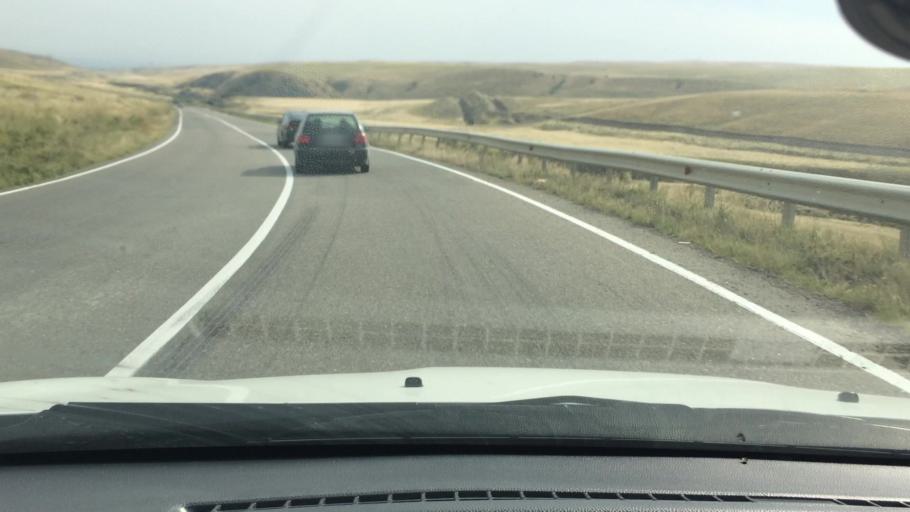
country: GE
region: Kvemo Kartli
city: Rust'avi
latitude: 41.5240
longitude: 44.9364
